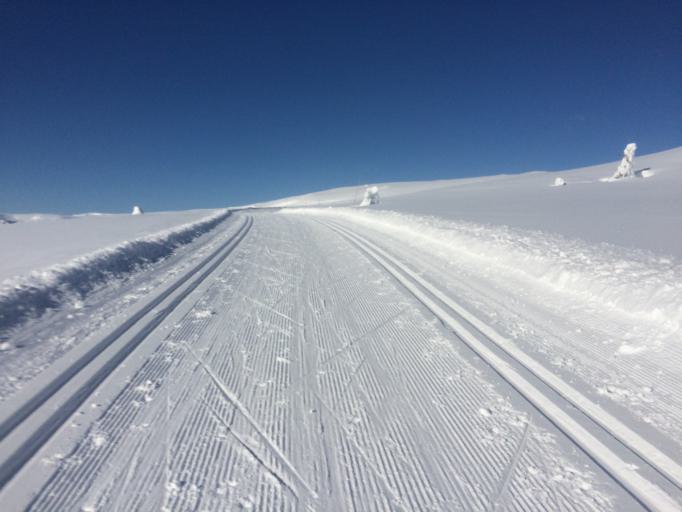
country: NO
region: Oppland
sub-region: Ringebu
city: Ringebu
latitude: 61.3678
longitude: 10.0747
